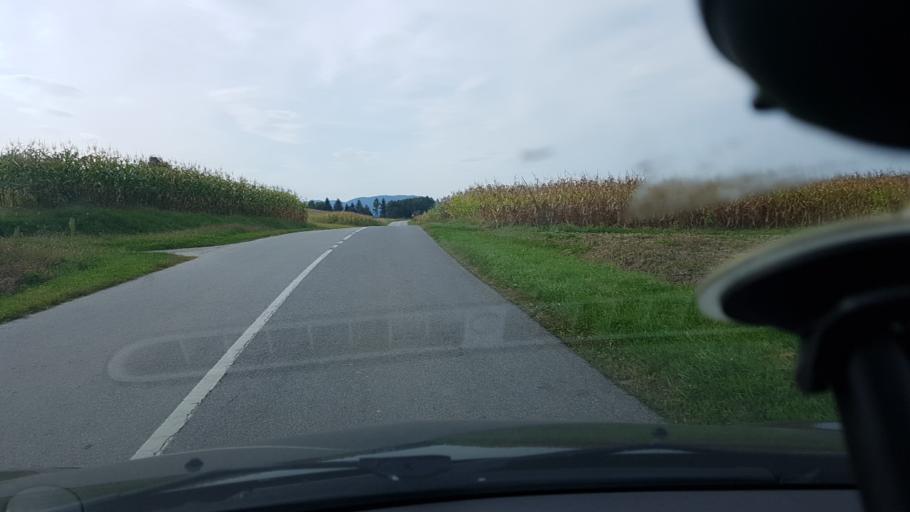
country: HR
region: Varazdinska
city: Ivanec
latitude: 46.2340
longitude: 16.1621
